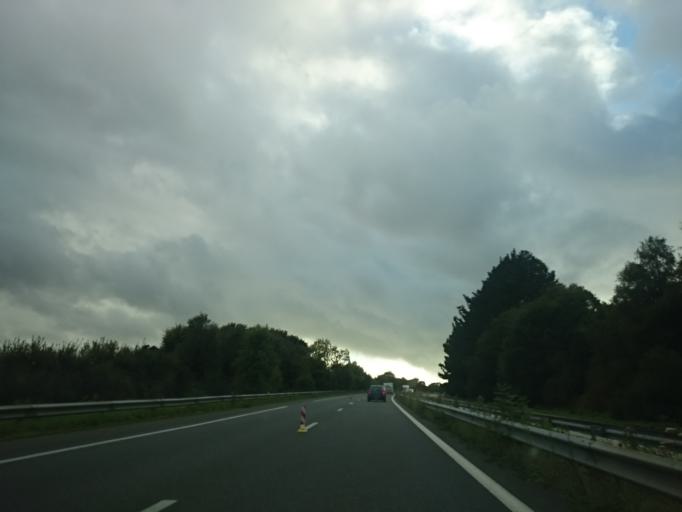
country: FR
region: Brittany
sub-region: Departement du Finistere
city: Plouigneau
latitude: 48.5739
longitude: -3.6612
